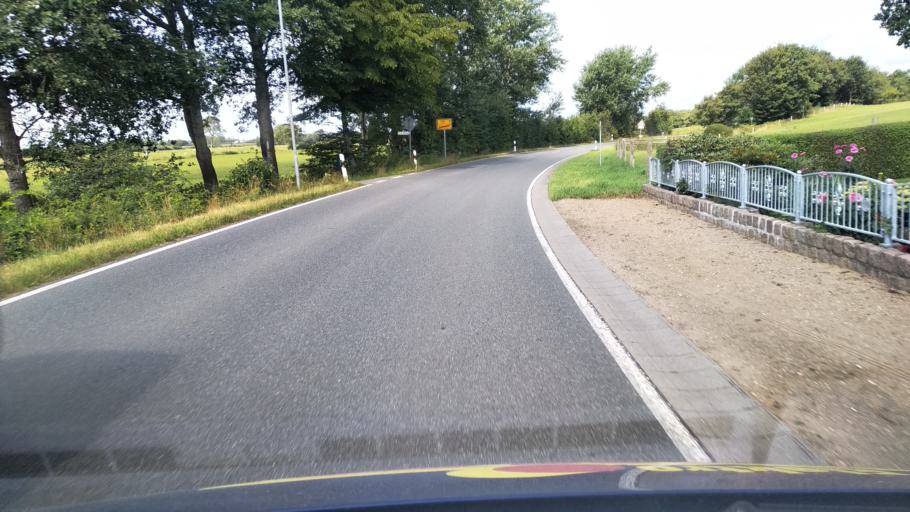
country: DE
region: Schleswig-Holstein
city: Brekendorf
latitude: 54.4228
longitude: 9.6219
